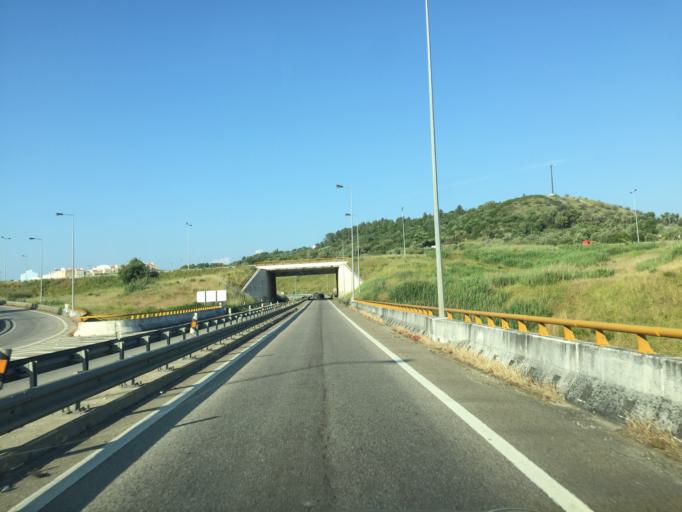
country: PT
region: Santarem
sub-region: Santarem
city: Santarem
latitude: 39.2299
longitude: -8.7070
